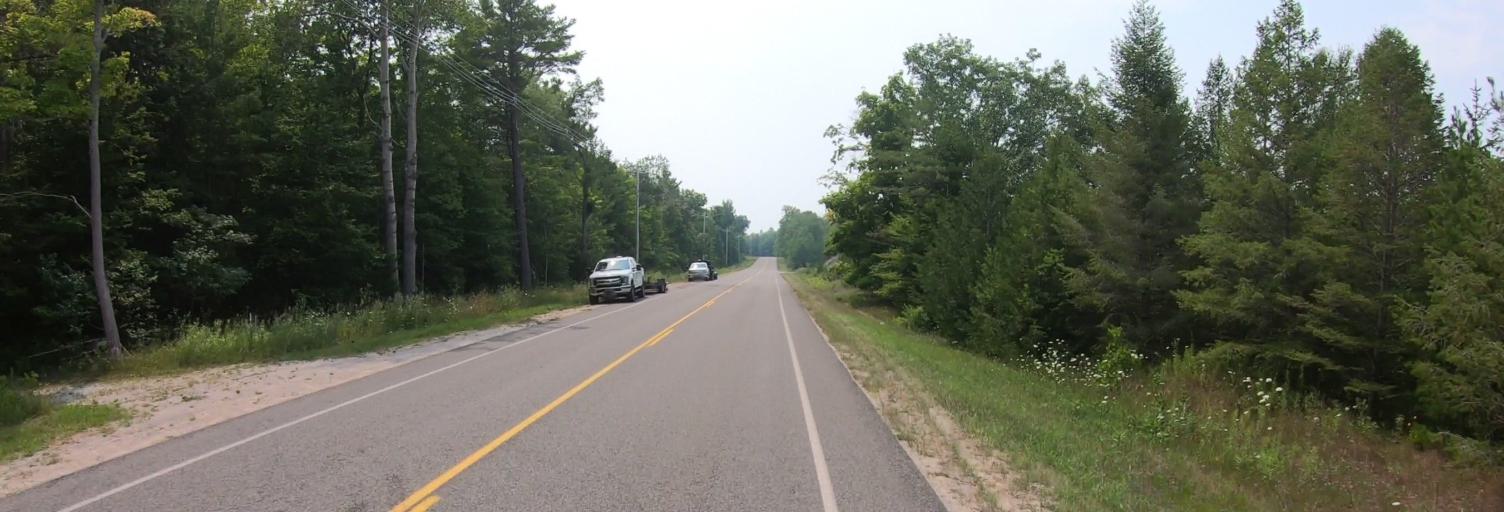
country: US
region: Michigan
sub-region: Leelanau County
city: Leland
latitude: 45.1710
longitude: -85.5555
